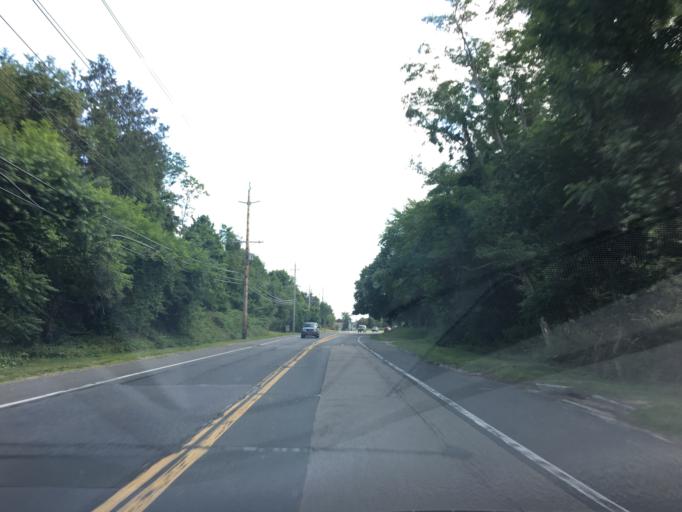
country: US
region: New York
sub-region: Suffolk County
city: Southold
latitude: 41.0783
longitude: -72.4242
